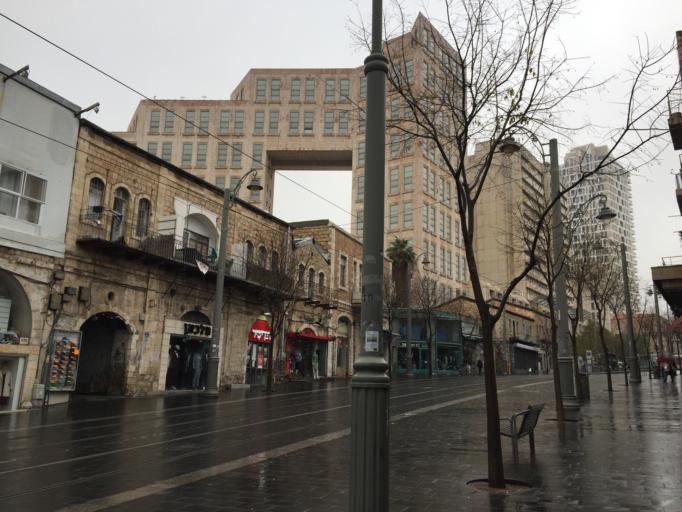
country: IL
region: Jerusalem
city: West Jerusalem
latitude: 31.7840
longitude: 35.2164
